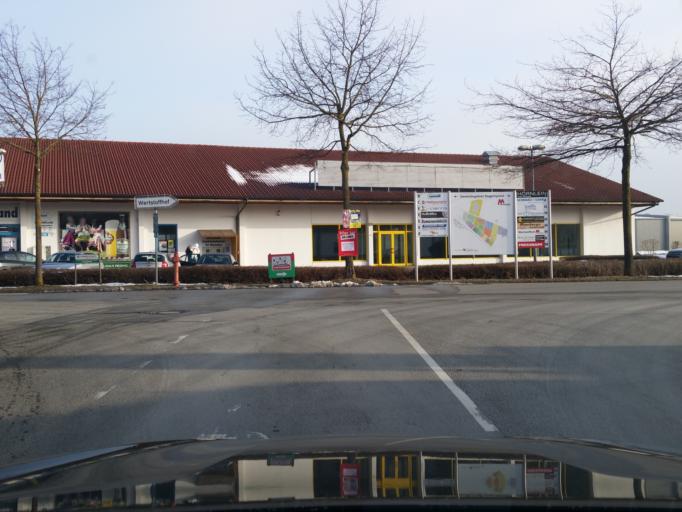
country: DE
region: Bavaria
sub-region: Upper Bavaria
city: Moosburg
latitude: 48.4706
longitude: 11.9639
